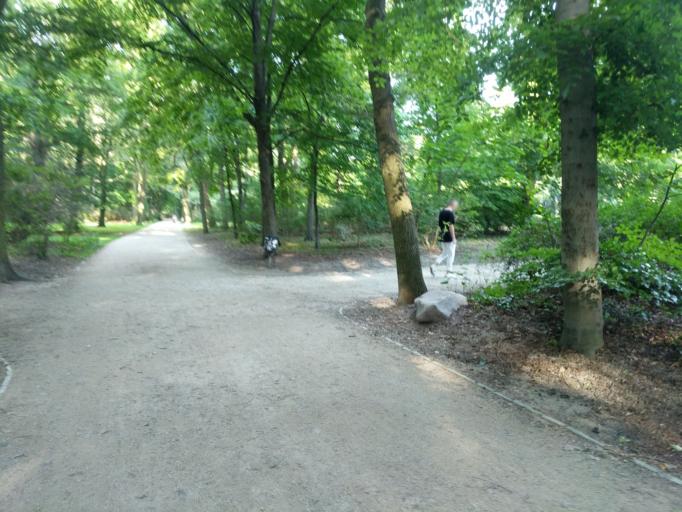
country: DE
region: Berlin
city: Tiergarten Bezirk
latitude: 52.5151
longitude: 13.3543
